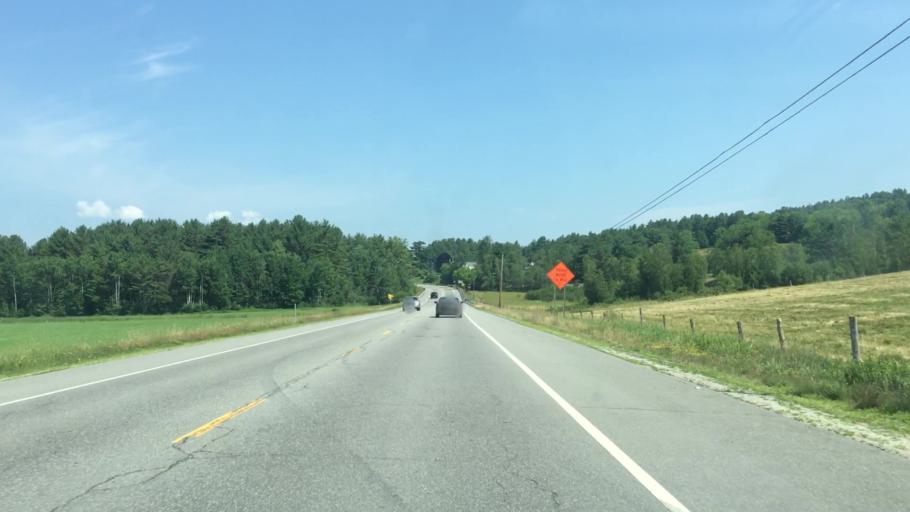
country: US
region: New Hampshire
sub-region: Sullivan County
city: Sunapee
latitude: 43.3656
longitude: -72.1209
